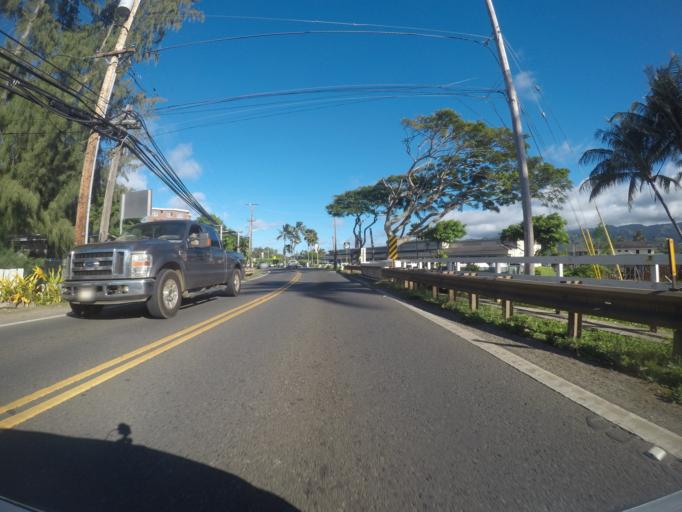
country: US
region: Hawaii
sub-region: Honolulu County
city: La'ie
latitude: 21.6480
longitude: -157.9228
